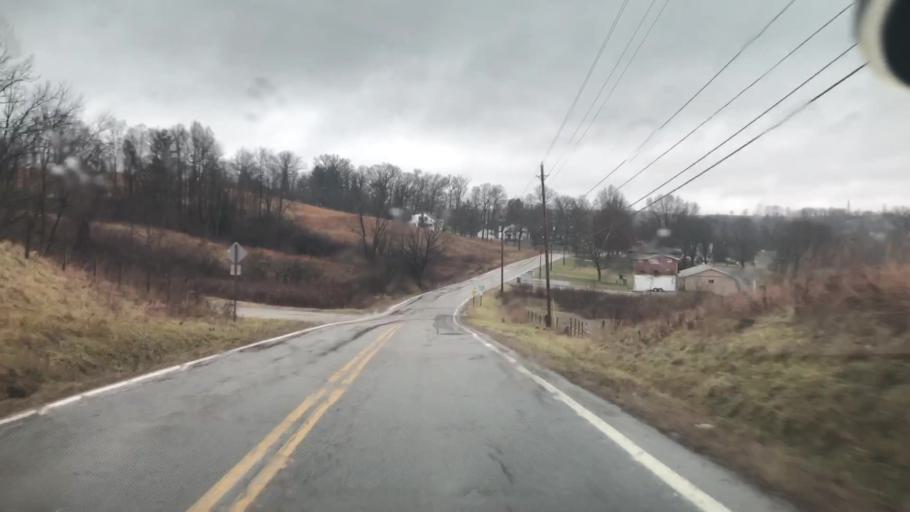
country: US
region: Ohio
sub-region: Harrison County
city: Cadiz
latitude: 40.2573
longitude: -81.0020
